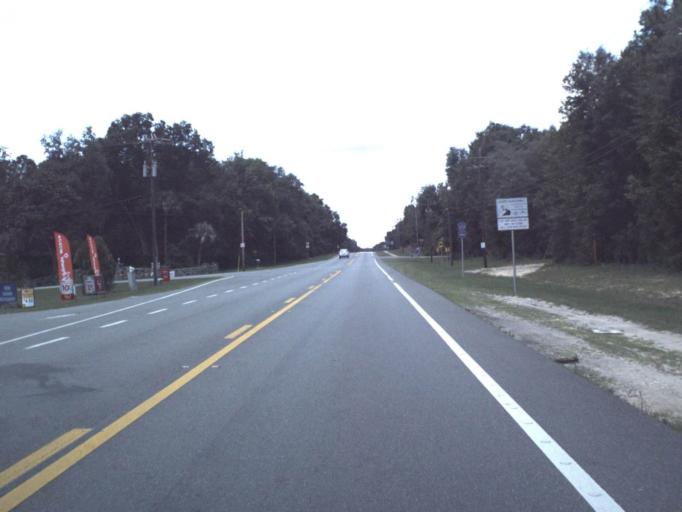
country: US
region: Florida
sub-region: Clay County
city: Keystone Heights
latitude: 29.7612
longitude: -82.0017
